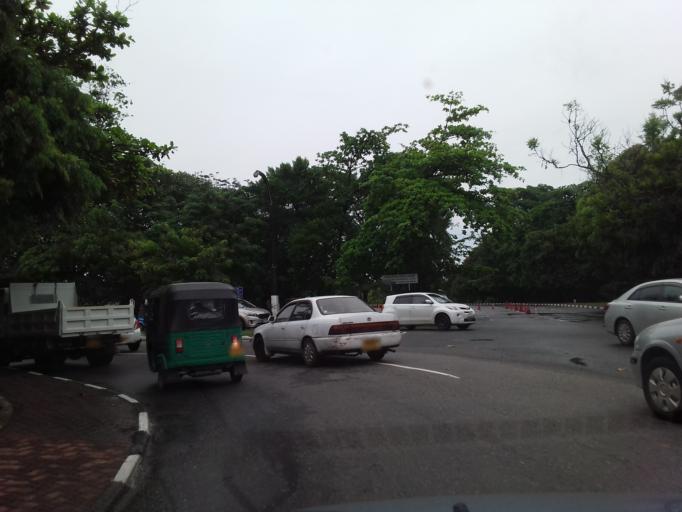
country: LK
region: Western
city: Battaramulla South
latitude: 6.8941
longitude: 79.9156
